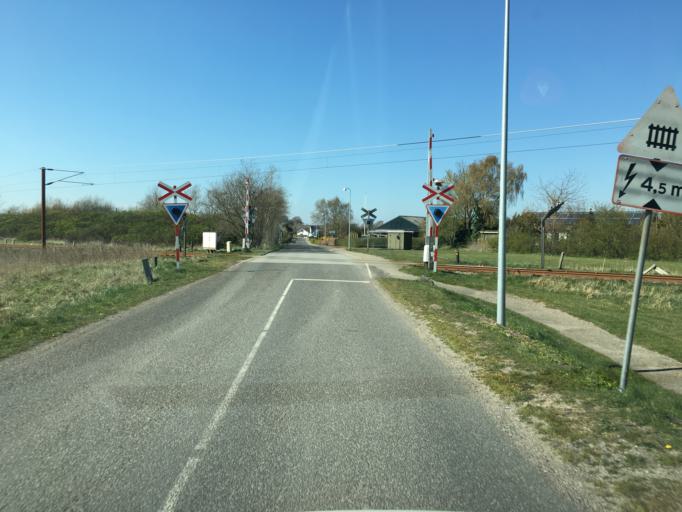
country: DK
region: South Denmark
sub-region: Aabenraa Kommune
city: Krusa
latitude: 54.9344
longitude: 9.4074
